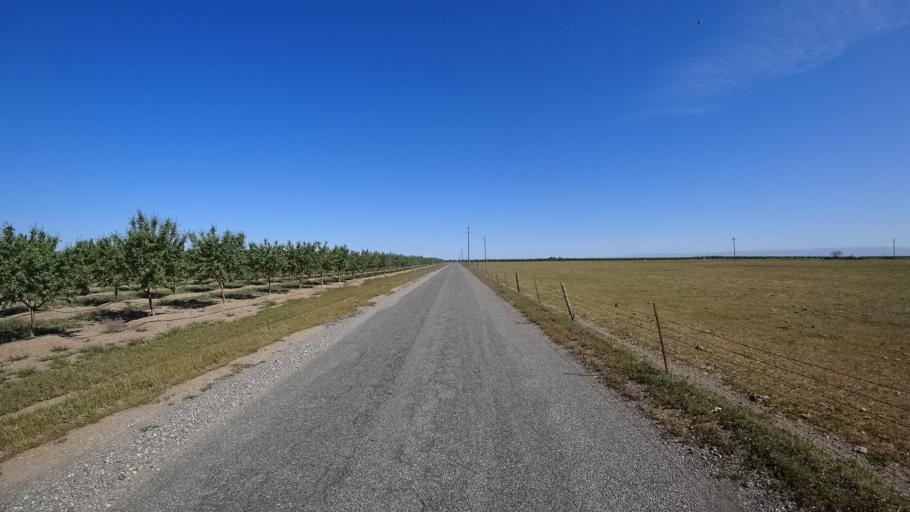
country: US
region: California
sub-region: Glenn County
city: Willows
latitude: 39.6194
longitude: -122.1564
